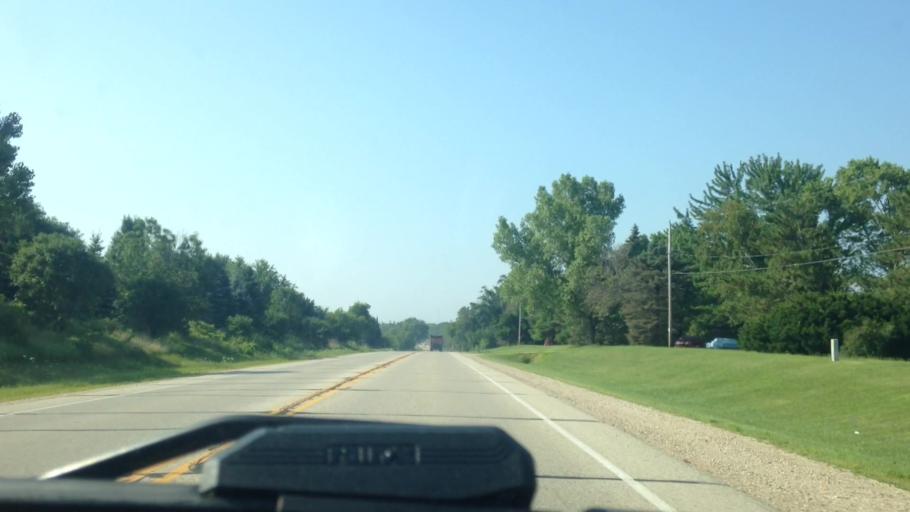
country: US
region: Wisconsin
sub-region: Waukesha County
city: Merton
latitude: 43.1894
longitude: -88.2617
